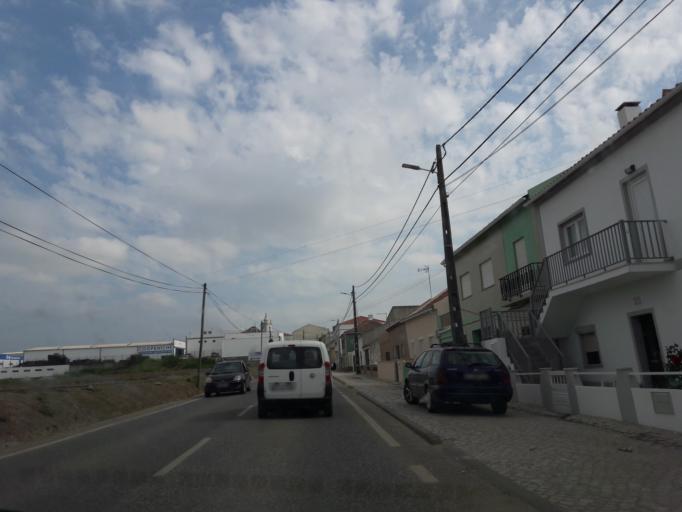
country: PT
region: Leiria
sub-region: Peniche
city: Atouguia da Baleia
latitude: 39.3421
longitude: -9.3278
